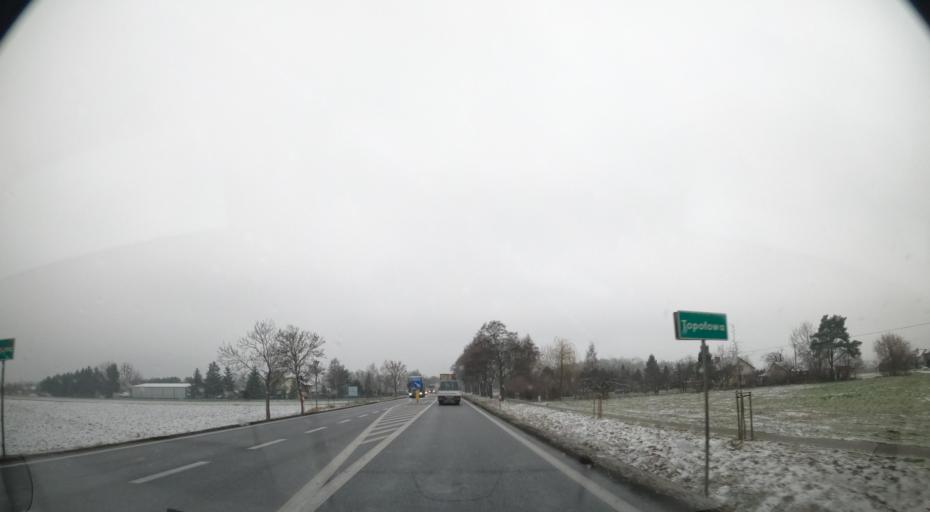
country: PL
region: Masovian Voivodeship
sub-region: Powiat sochaczewski
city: Teresin
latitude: 52.2149
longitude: 20.3975
